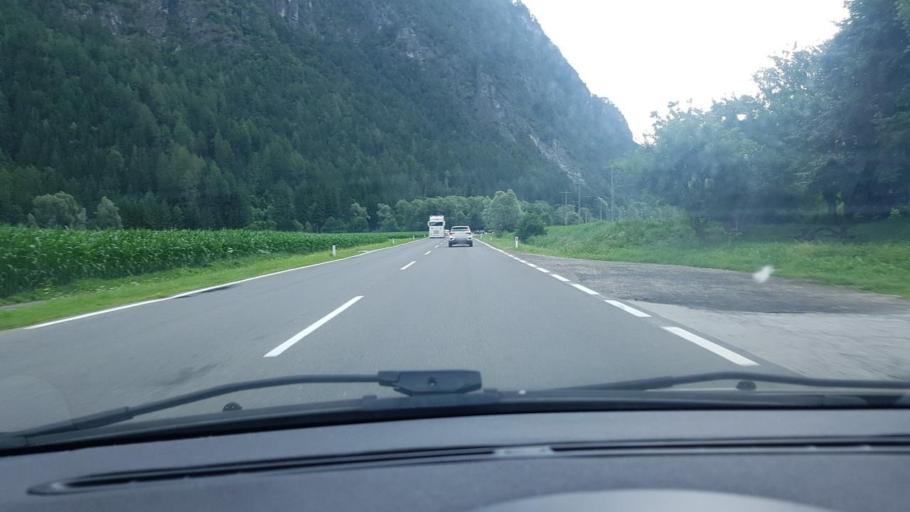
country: AT
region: Tyrol
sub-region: Politischer Bezirk Lienz
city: Nikolsdorf
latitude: 46.7667
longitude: 12.9274
